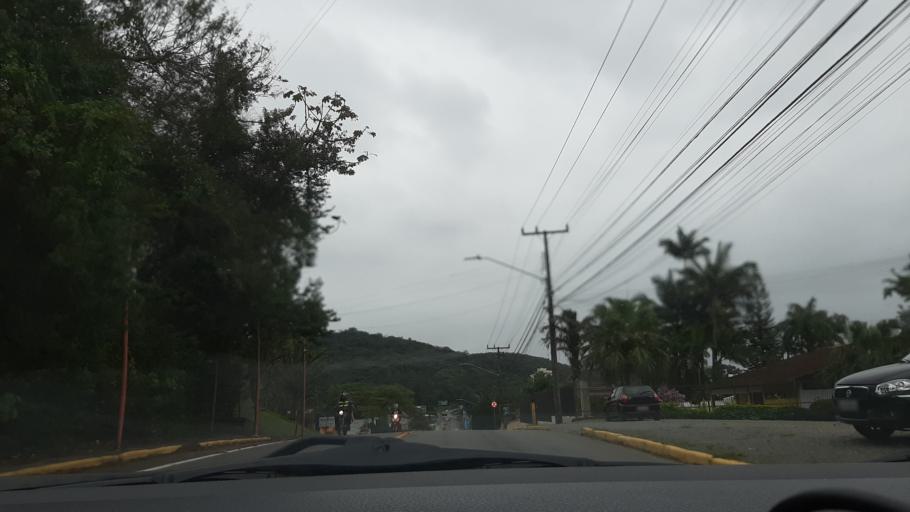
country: BR
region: Santa Catarina
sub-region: Joinville
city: Joinville
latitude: -26.3168
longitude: -48.8588
